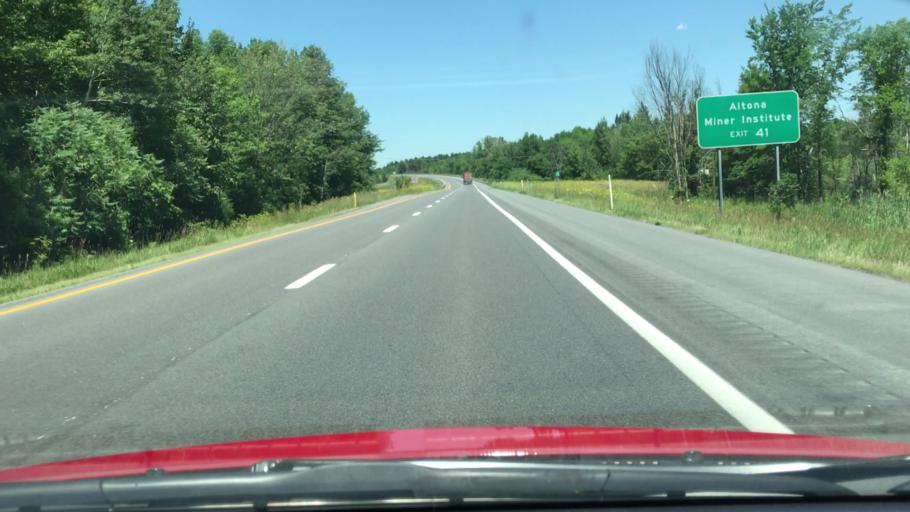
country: US
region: New York
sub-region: Clinton County
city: Champlain
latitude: 44.8774
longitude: -73.4511
